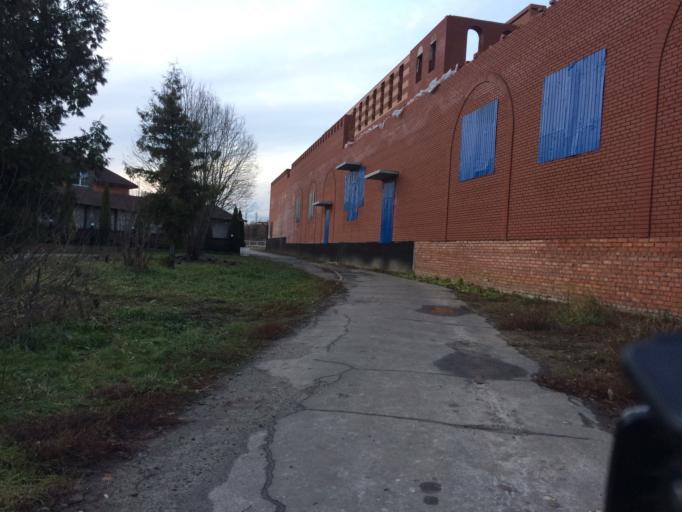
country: RU
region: Mariy-El
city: Yoshkar-Ola
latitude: 56.6263
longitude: 47.9042
